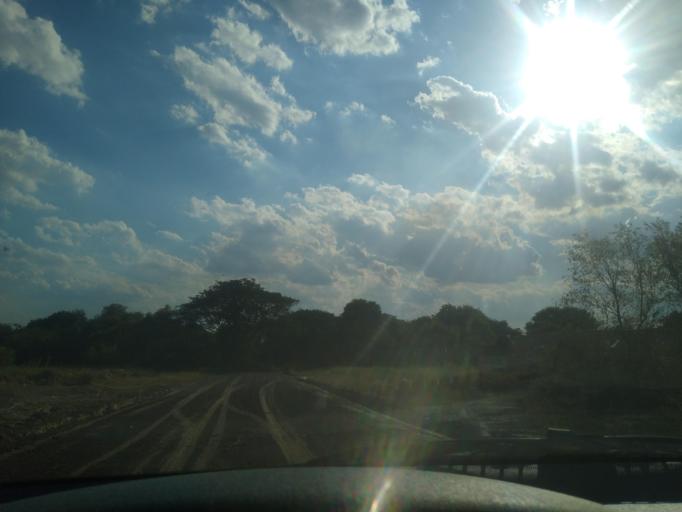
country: AR
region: Chaco
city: Resistencia
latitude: -27.4183
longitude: -58.9451
